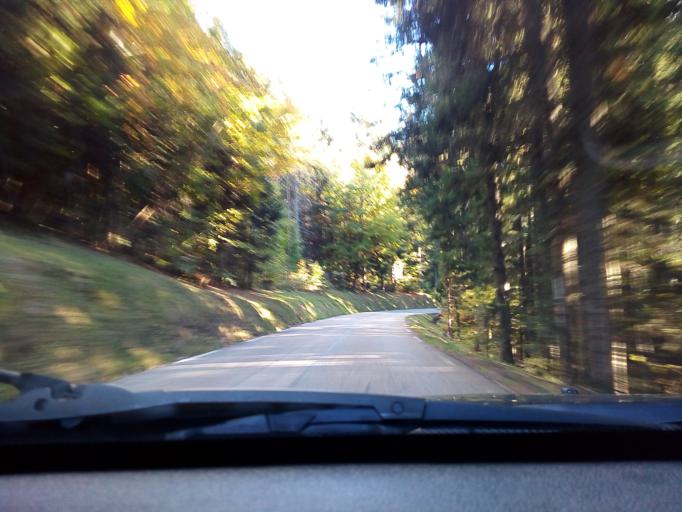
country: FR
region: Rhone-Alpes
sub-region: Departement de l'Isere
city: Le Sappey-en-Chartreuse
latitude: 45.2780
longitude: 5.7663
